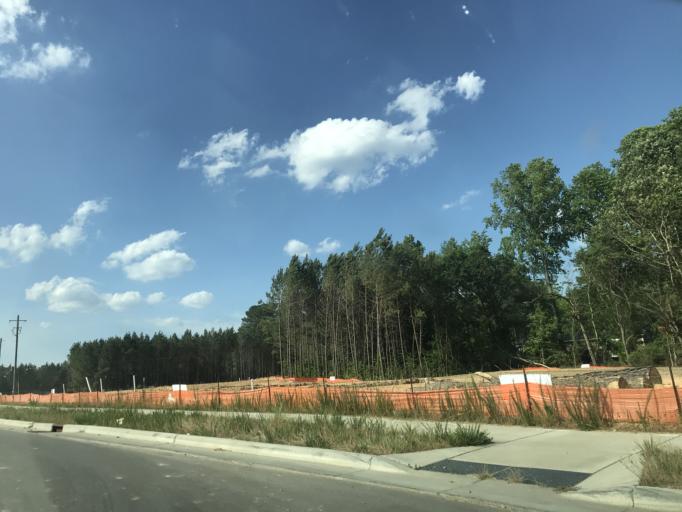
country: US
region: North Carolina
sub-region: Wake County
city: Garner
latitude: 35.7212
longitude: -78.5598
